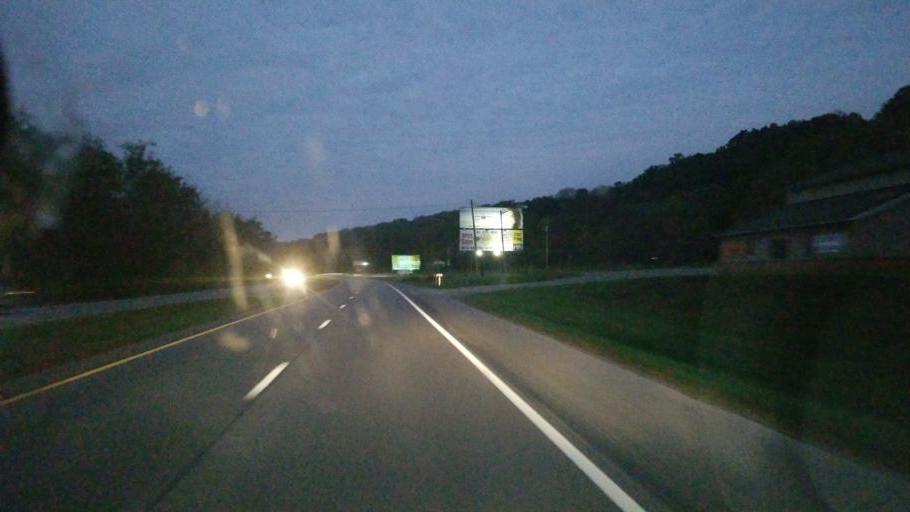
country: US
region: Ohio
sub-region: Ross County
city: Chillicothe
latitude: 39.2581
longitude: -82.9734
